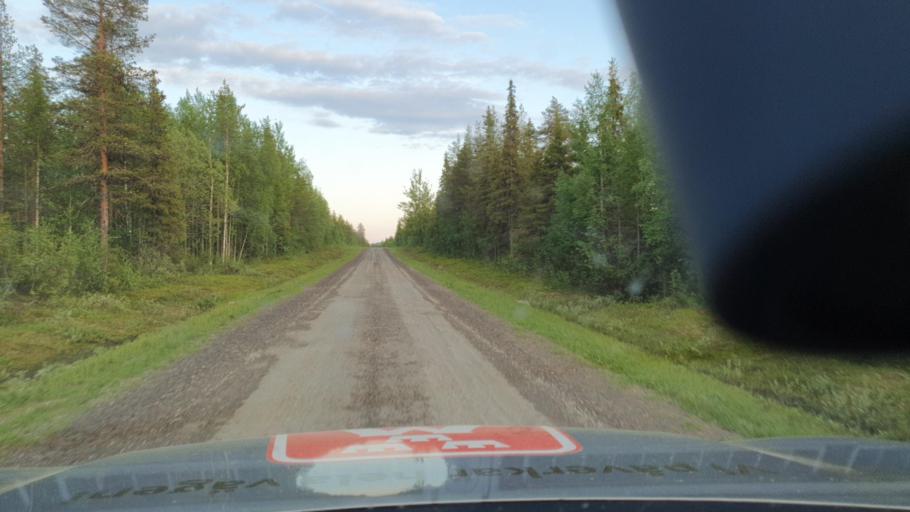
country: SE
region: Norrbotten
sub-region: Bodens Kommun
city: Boden
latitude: 66.5017
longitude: 21.5509
